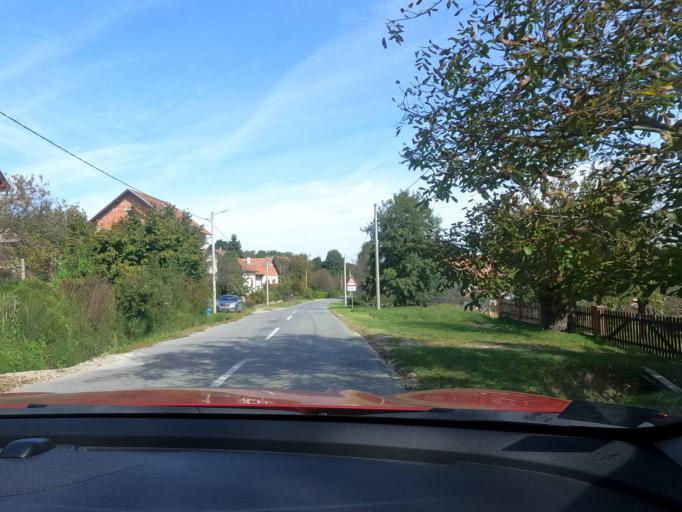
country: HR
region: Sisacko-Moslavacka
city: Petrinja
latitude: 45.4032
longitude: 16.2896
